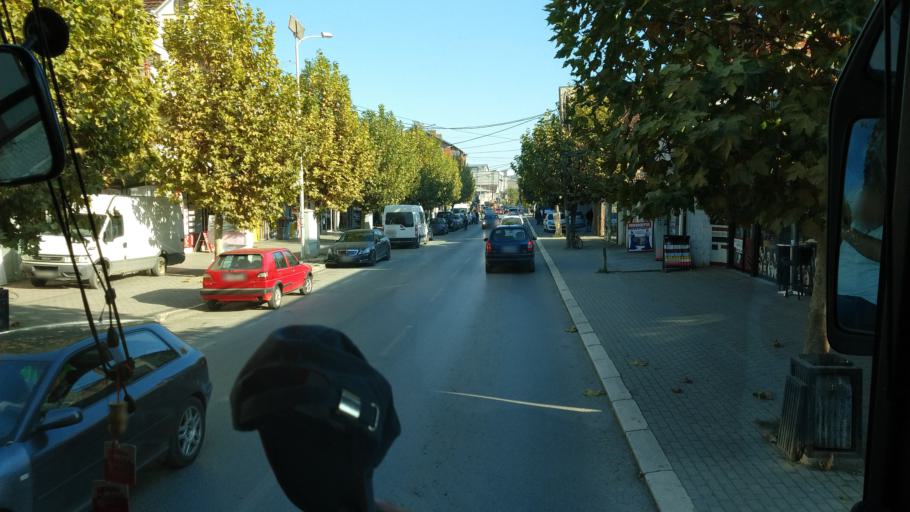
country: XK
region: Ferizaj
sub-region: Komuna e Shtimes
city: Shtime
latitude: 42.4344
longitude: 21.0357
